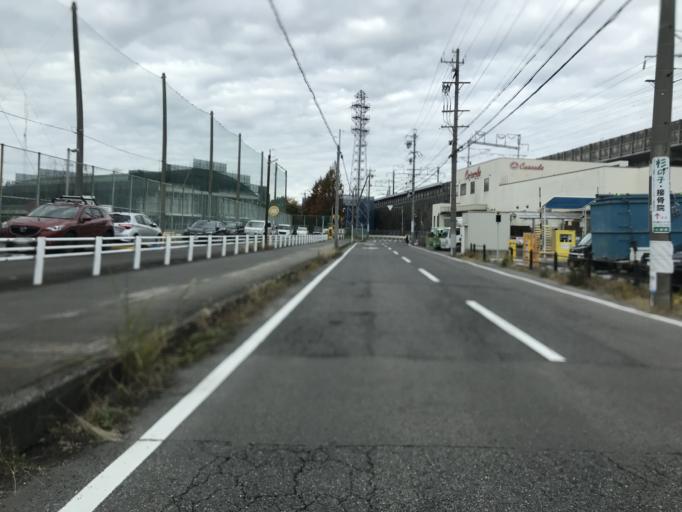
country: JP
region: Aichi
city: Nagoya-shi
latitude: 35.1999
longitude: 136.8598
